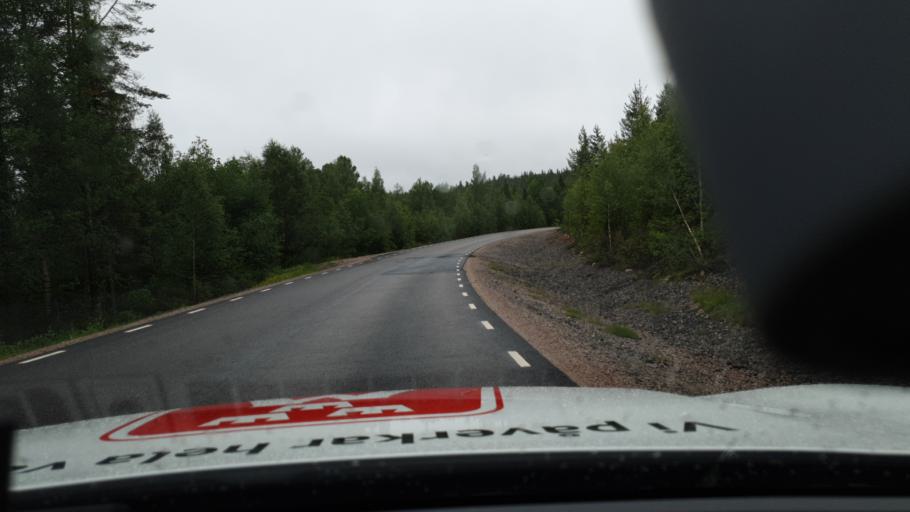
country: SE
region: Norrbotten
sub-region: Overtornea Kommun
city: OEvertornea
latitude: 66.5139
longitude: 23.3864
